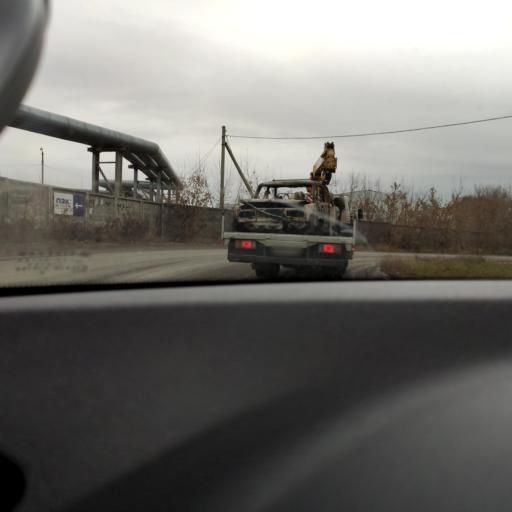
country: RU
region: Samara
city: Smyshlyayevka
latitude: 53.2067
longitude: 50.3024
